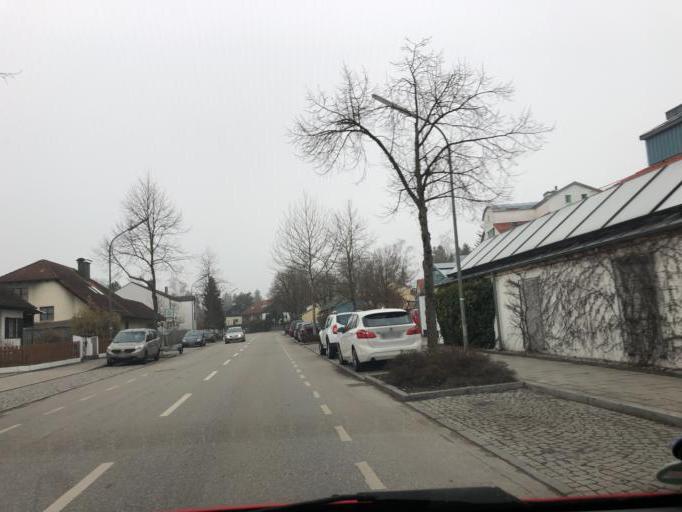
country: DE
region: Bavaria
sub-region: Upper Bavaria
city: Grobenzell
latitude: 48.1959
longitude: 11.3788
